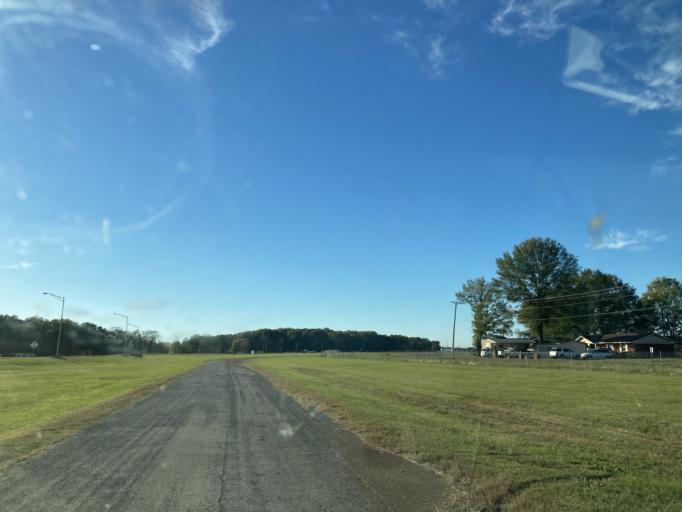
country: US
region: Mississippi
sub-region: Yazoo County
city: Yazoo City
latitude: 32.8796
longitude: -90.4181
